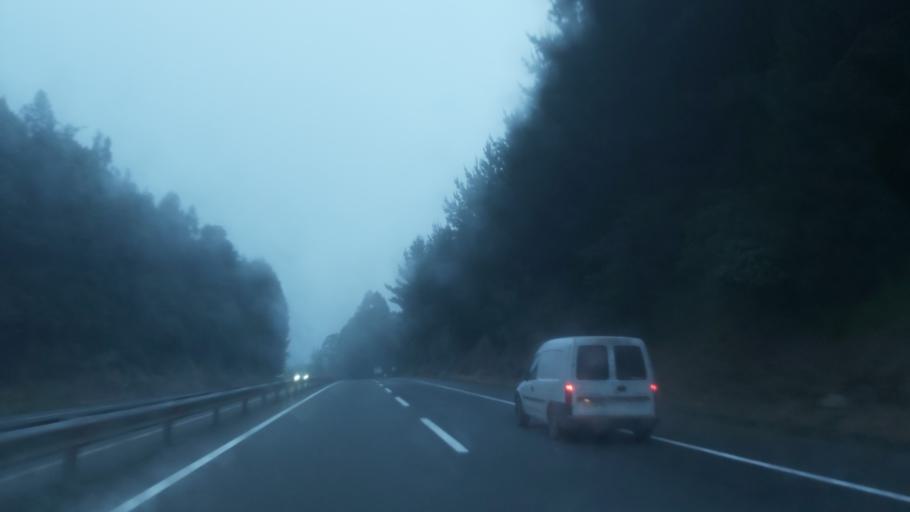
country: CL
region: Biobio
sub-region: Provincia de Concepcion
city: Penco
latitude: -36.7421
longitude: -72.9073
